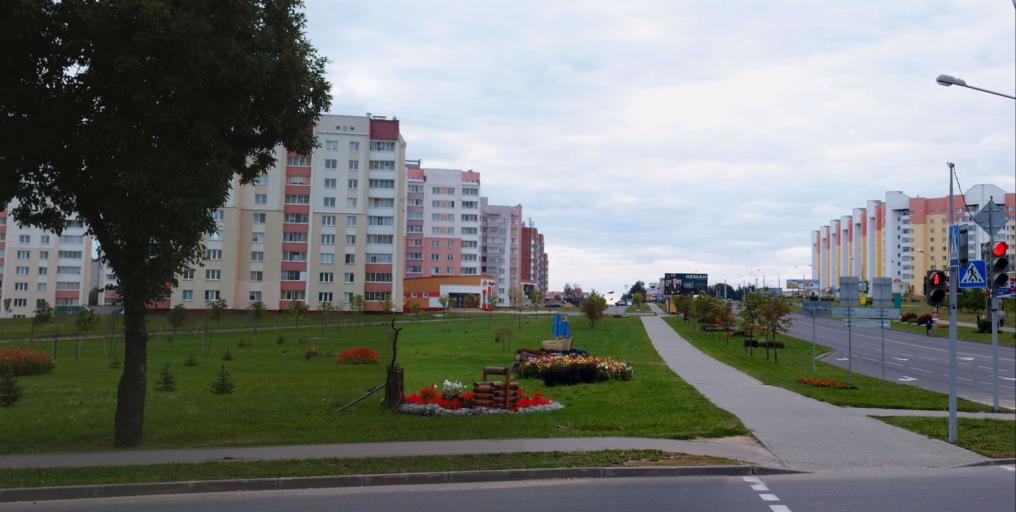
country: BY
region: Minsk
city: Maladzyechna
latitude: 54.2990
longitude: 26.8700
